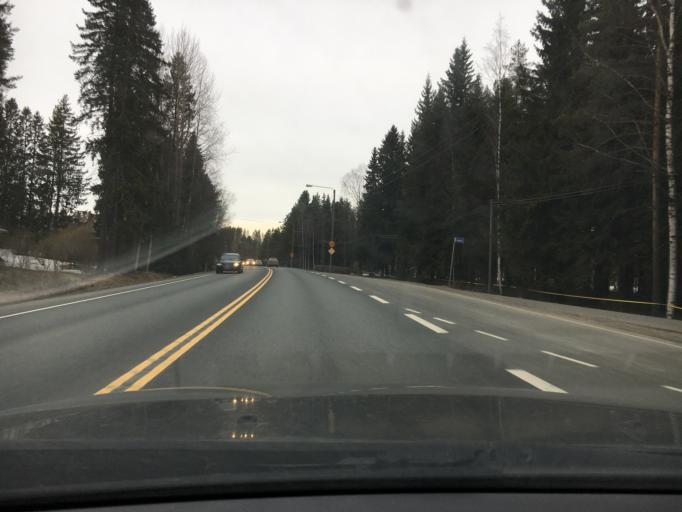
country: FI
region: Northern Savo
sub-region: Kuopio
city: Siilinjaervi
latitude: 63.1150
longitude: 27.6420
